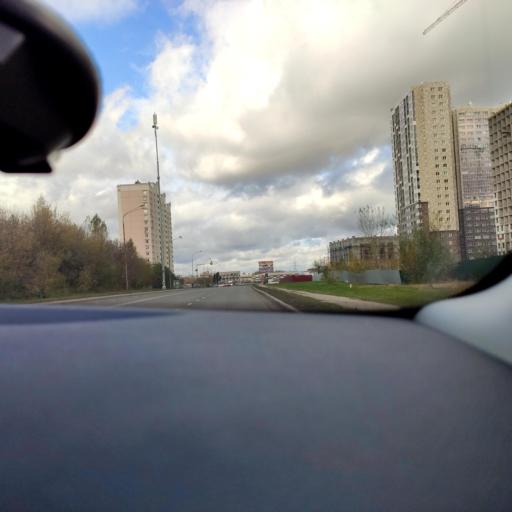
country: RU
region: Moskovskaya
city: Kotel'niki
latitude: 55.6368
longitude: 37.8482
